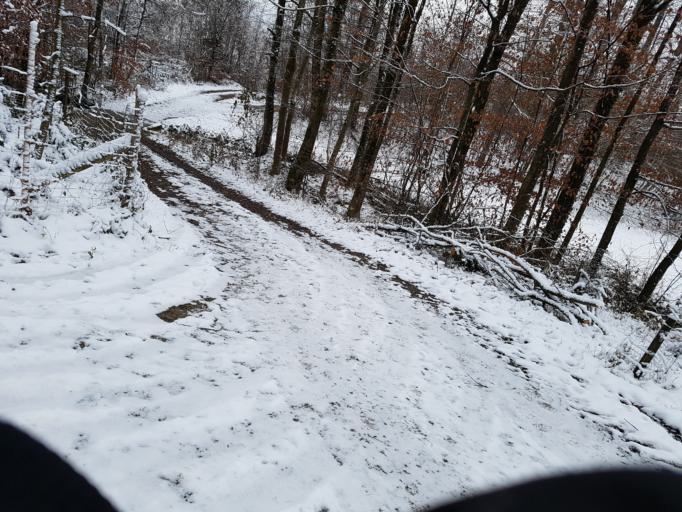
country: AT
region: Salzburg
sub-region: Politischer Bezirk Hallein
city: Puch bei Hallein
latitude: 47.7277
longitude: 13.0971
